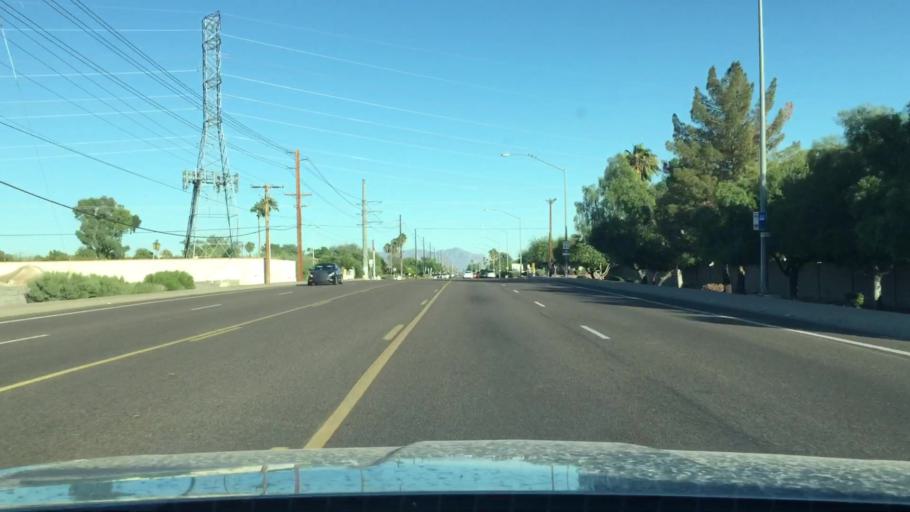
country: US
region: Arizona
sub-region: Maricopa County
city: Gilbert
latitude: 33.4082
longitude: -111.7480
